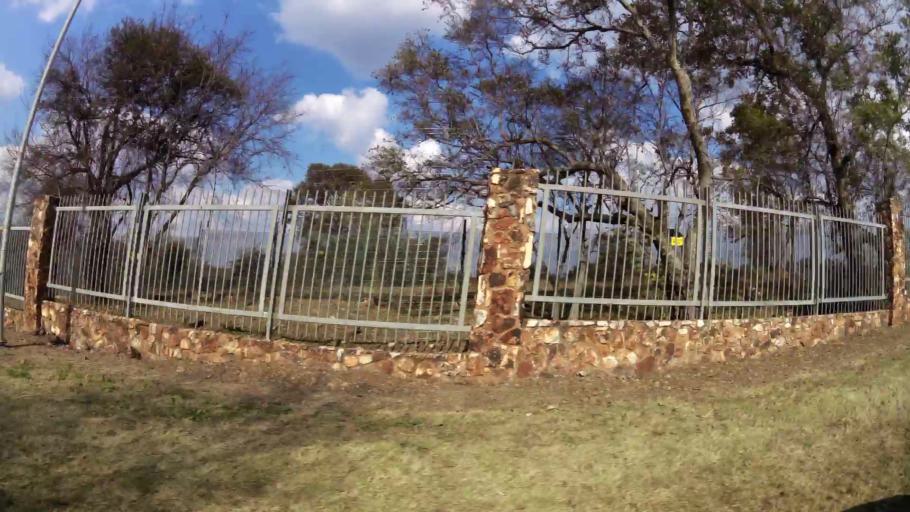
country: ZA
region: Gauteng
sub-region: City of Tshwane Metropolitan Municipality
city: Centurion
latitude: -25.8796
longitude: 28.2065
